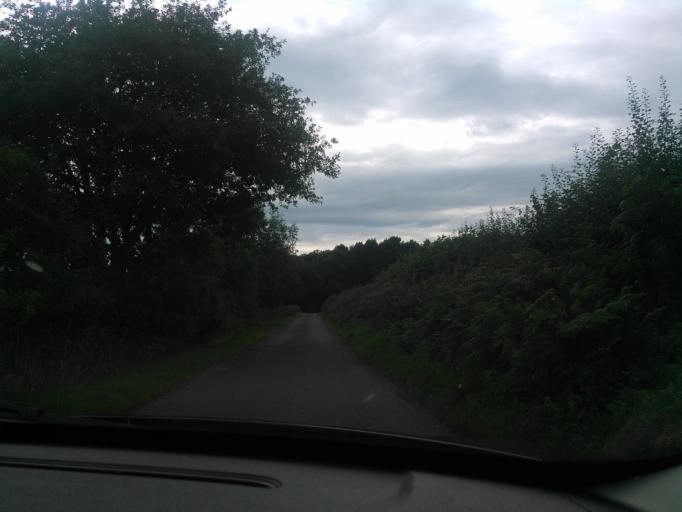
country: GB
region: England
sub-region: Shropshire
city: Shawbury
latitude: 52.8366
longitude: -2.6073
